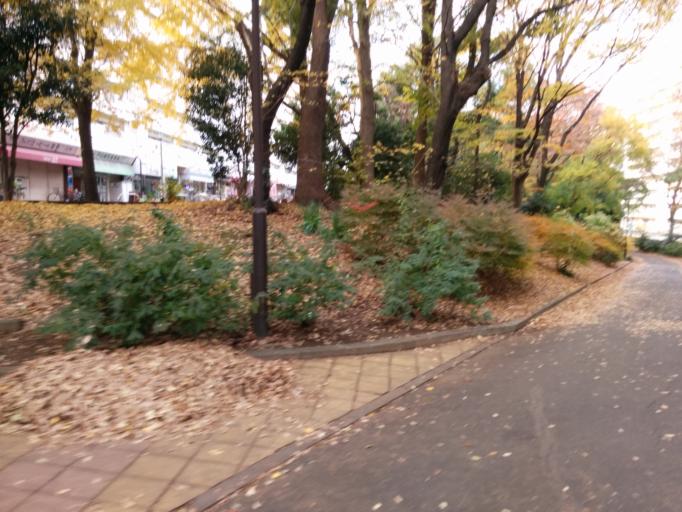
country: JP
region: Tokyo
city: Tokyo
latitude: 35.7011
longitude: 139.7097
